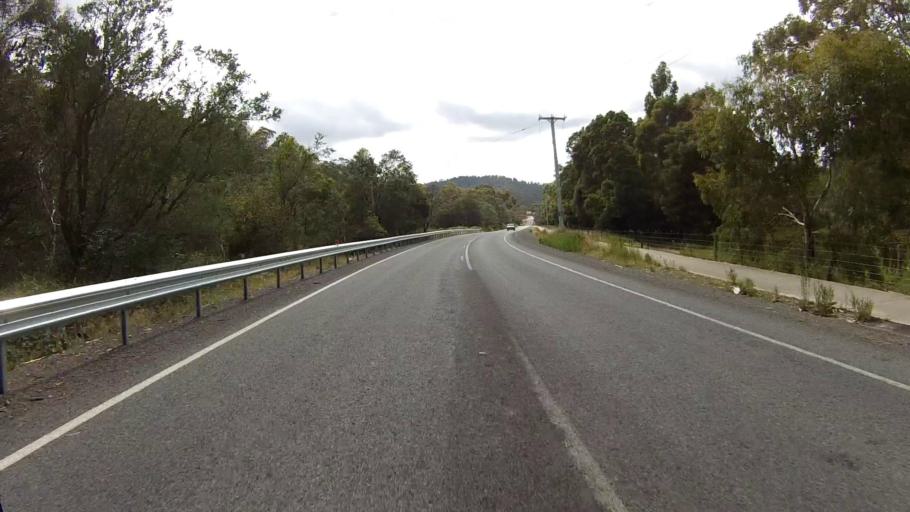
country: AU
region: Tasmania
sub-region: Glenorchy
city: Lutana
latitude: -42.8079
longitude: 147.3401
